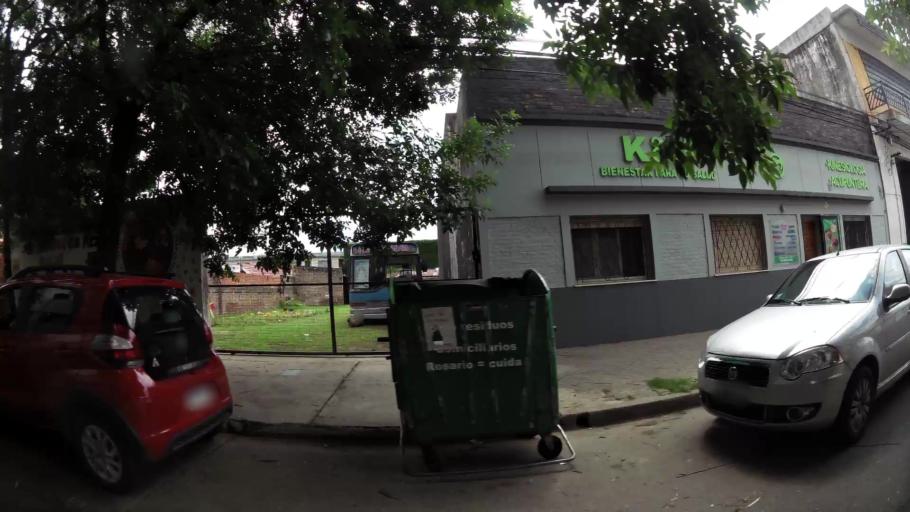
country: AR
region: Santa Fe
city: Gobernador Galvez
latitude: -32.9987
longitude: -60.6320
